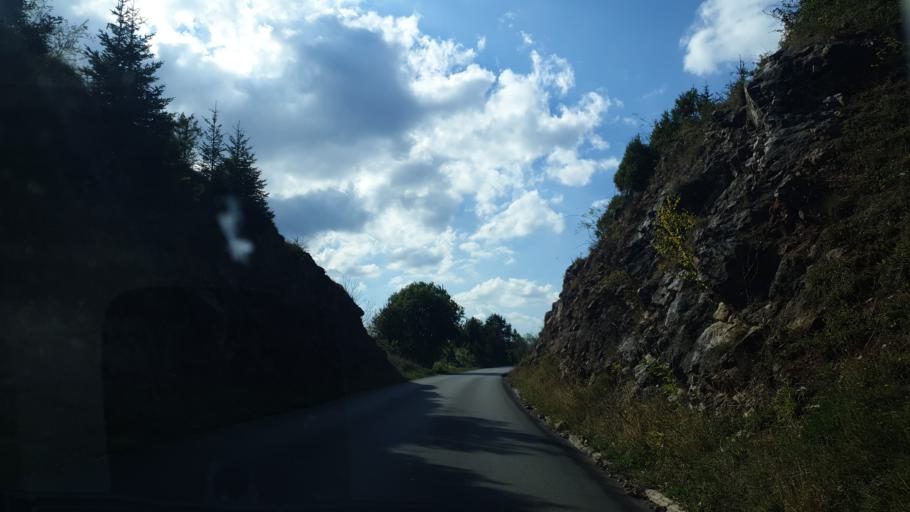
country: RS
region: Central Serbia
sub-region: Zlatiborski Okrug
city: Nova Varos
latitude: 43.4260
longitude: 19.9011
